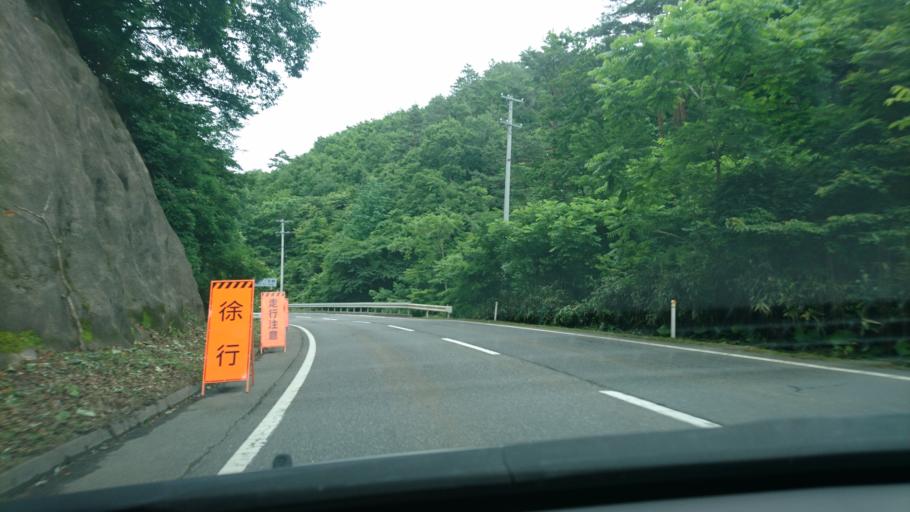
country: JP
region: Iwate
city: Miyako
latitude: 39.9676
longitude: 141.8601
